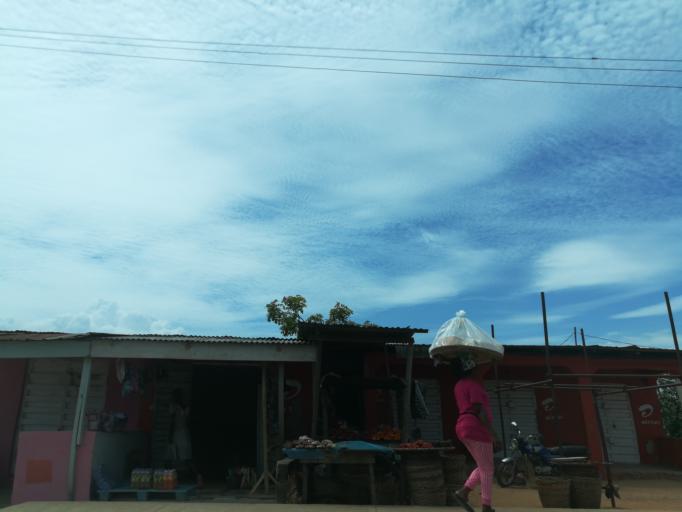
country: NG
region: Lagos
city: Ebute Ikorodu
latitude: 6.5690
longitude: 3.4808
